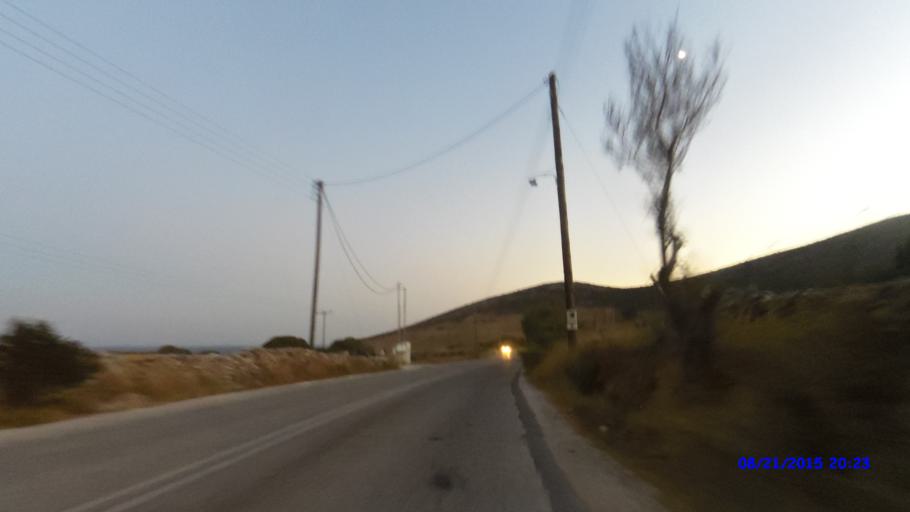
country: GR
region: South Aegean
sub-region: Nomos Kykladon
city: Antiparos
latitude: 36.9953
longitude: 25.0710
